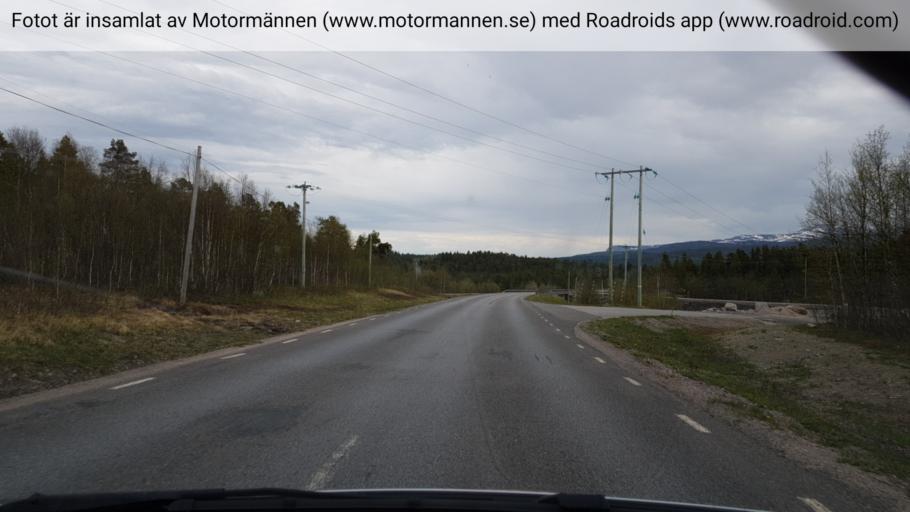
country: SE
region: Norrbotten
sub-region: Arjeplogs Kommun
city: Arjeplog
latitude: 66.4391
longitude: 16.8362
